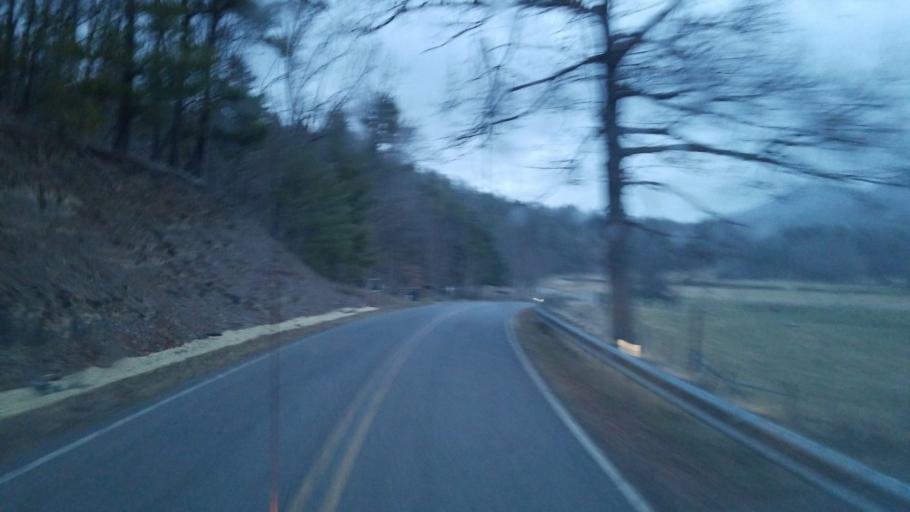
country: US
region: Virginia
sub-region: Pulaski County
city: Pulaski
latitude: 37.1127
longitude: -80.8857
